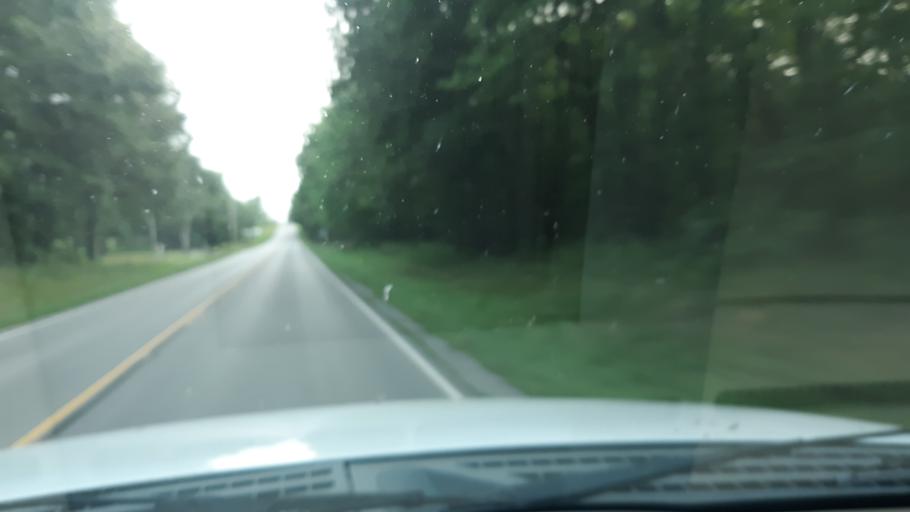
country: US
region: Illinois
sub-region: White County
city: Norris City
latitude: 37.9600
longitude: -88.3351
